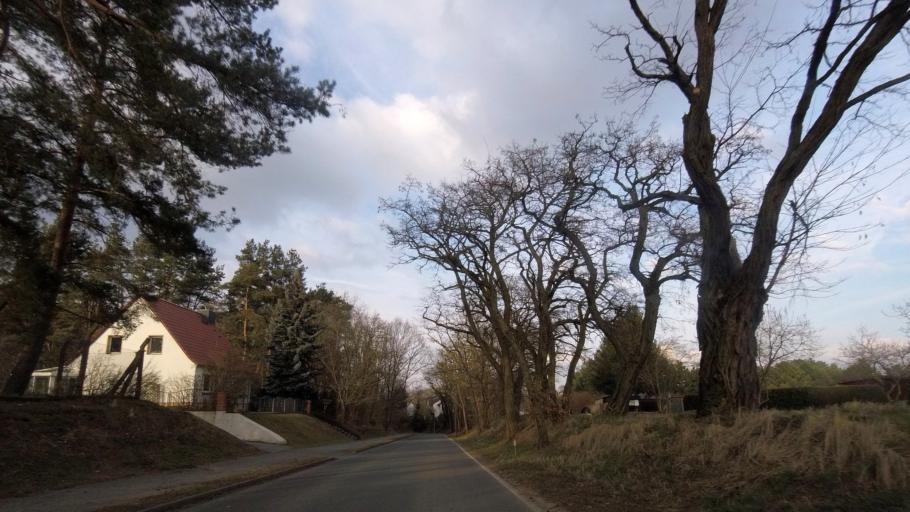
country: DE
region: Brandenburg
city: Belzig
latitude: 52.1322
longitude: 12.5863
